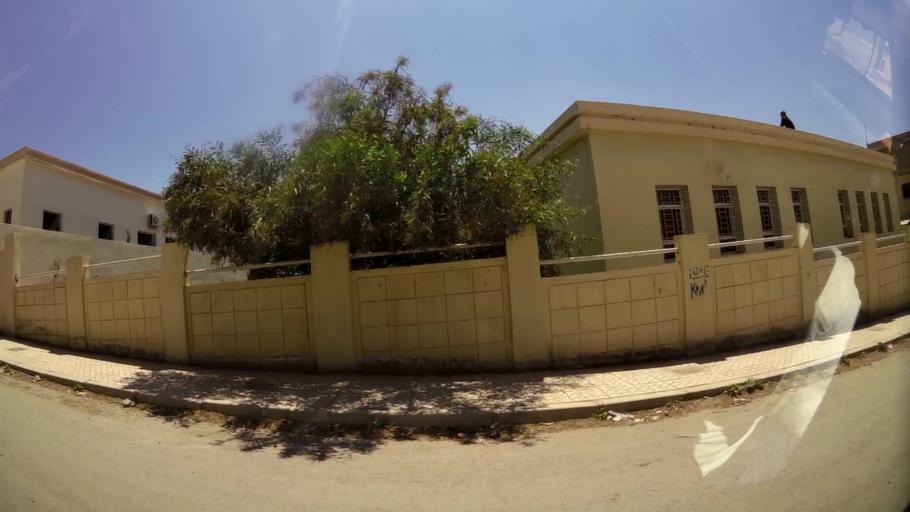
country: MA
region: Oriental
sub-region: Oujda-Angad
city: Oujda
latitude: 34.6906
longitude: -1.9481
